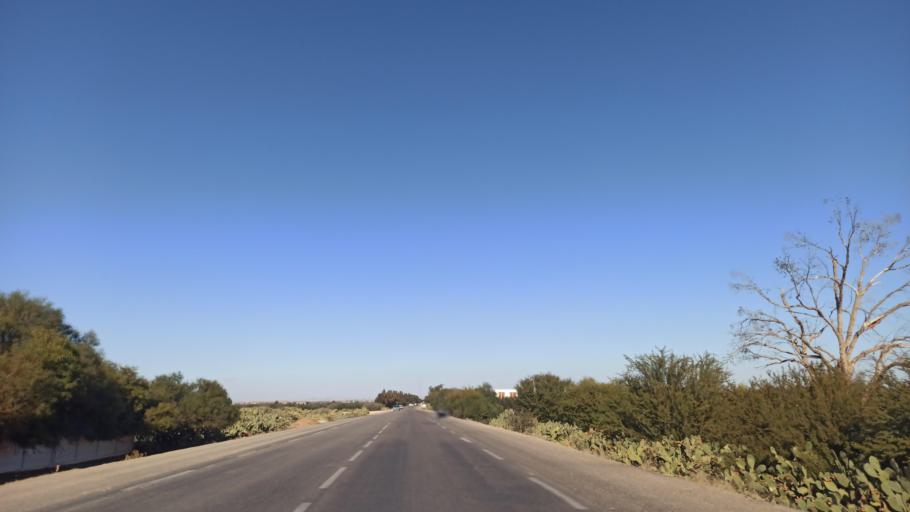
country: TN
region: Sidi Bu Zayd
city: Jilma
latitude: 35.1501
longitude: 9.3640
